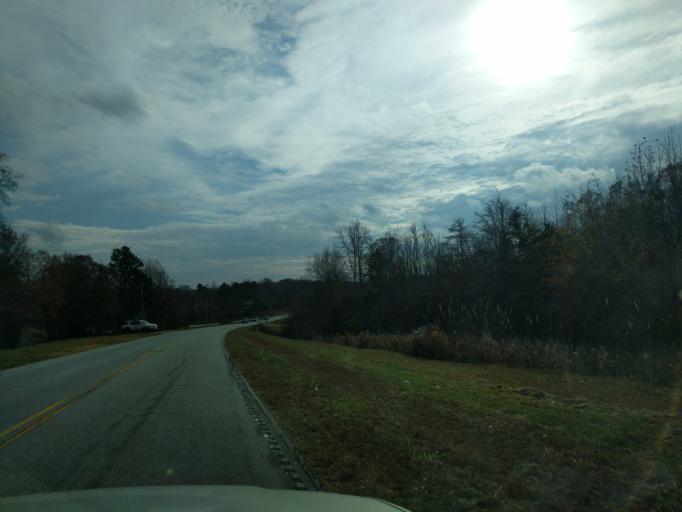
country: US
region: Georgia
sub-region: Franklin County
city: Gumlog
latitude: 34.5702
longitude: -83.0487
